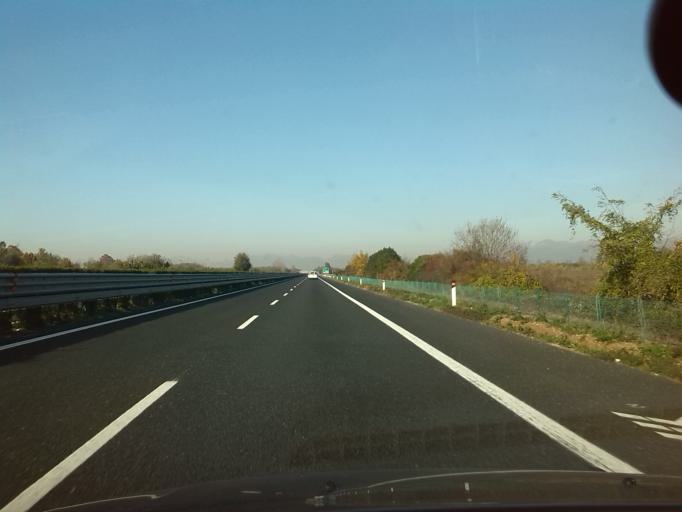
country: IT
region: Friuli Venezia Giulia
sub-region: Provincia di Udine
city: Zugliano-Terenzano-Cargnacco
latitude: 45.9919
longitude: 13.2358
